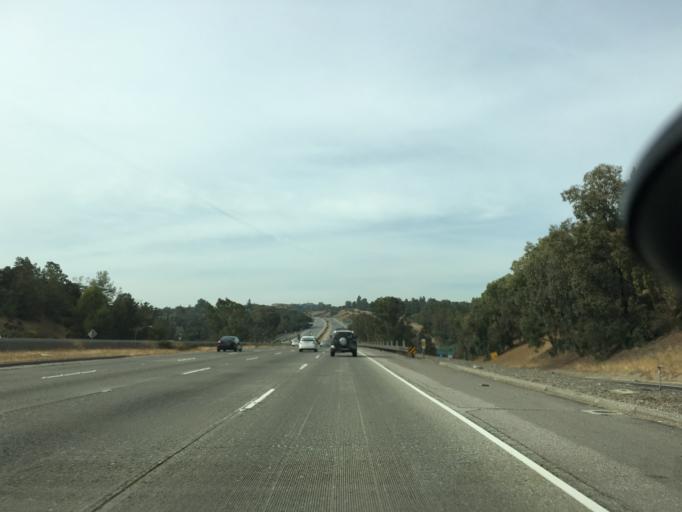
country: US
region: California
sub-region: San Mateo County
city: Woodside
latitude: 37.4333
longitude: -122.2406
